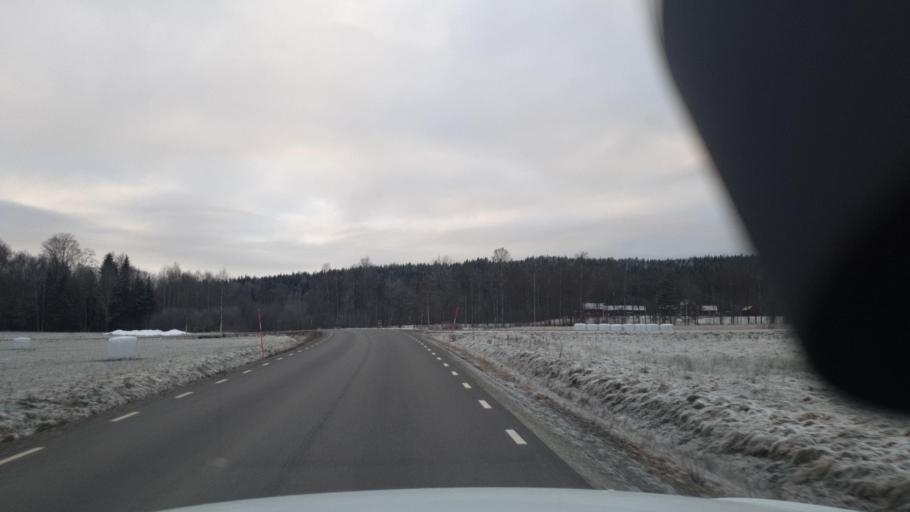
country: SE
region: Vaermland
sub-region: Torsby Kommun
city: Torsby
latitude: 59.9883
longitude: 12.8452
